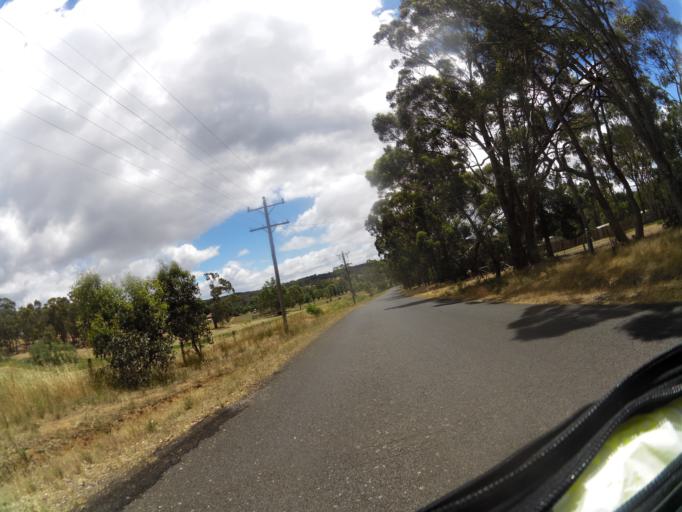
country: AU
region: Victoria
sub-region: Mount Alexander
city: Castlemaine
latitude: -37.0152
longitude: 144.2521
